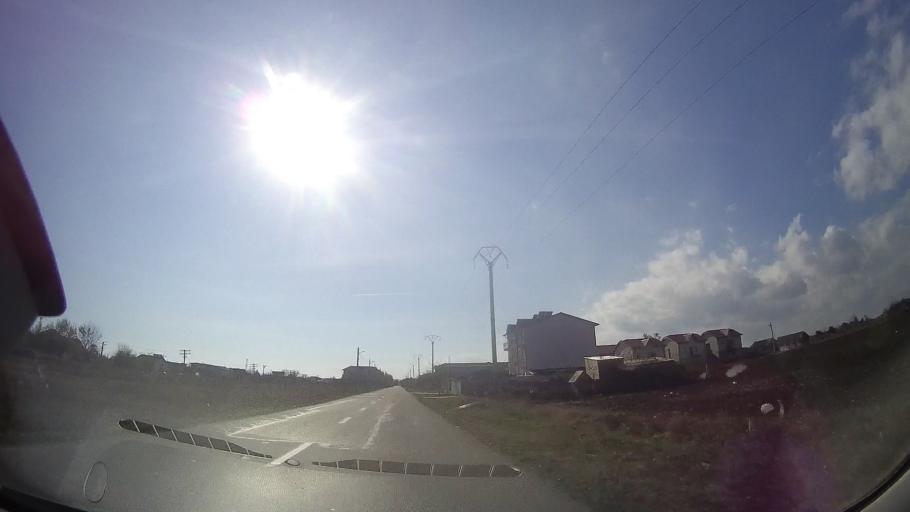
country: RO
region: Constanta
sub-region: Comuna Costinesti
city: Costinesti
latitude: 43.9582
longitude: 28.6347
